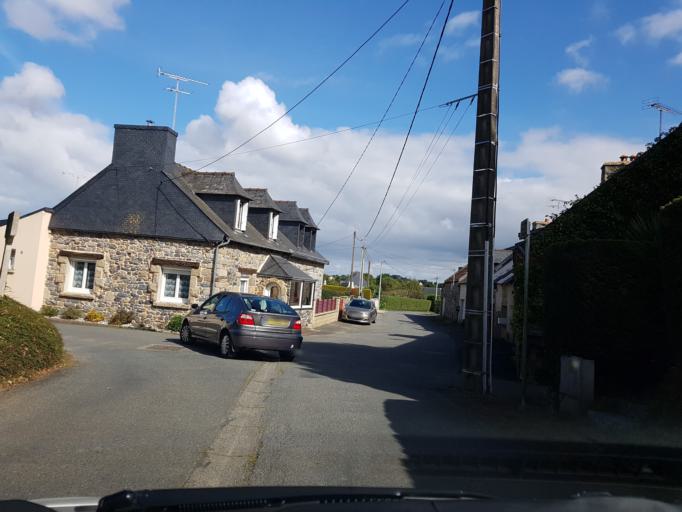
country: FR
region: Brittany
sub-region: Departement des Cotes-d'Armor
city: Pledran
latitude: 48.4691
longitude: -2.7633
